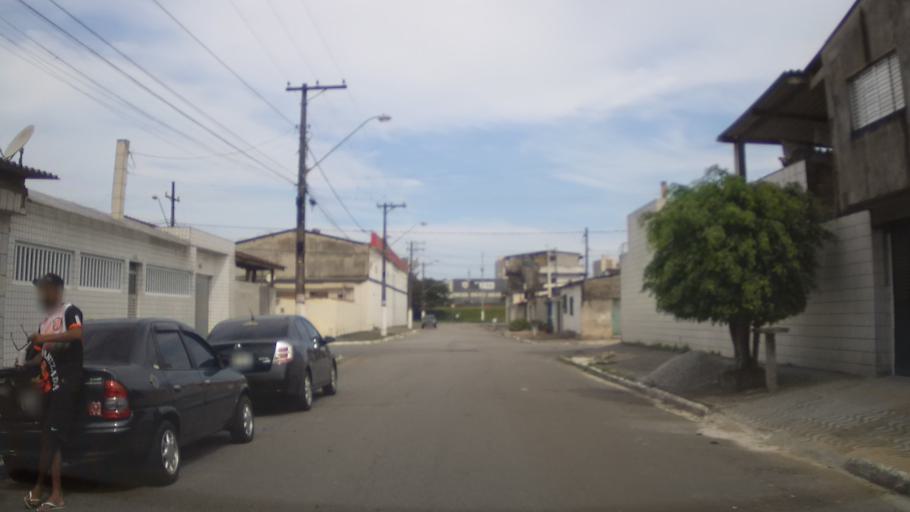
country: BR
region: Sao Paulo
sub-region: Praia Grande
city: Praia Grande
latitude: -24.0076
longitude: -46.4393
